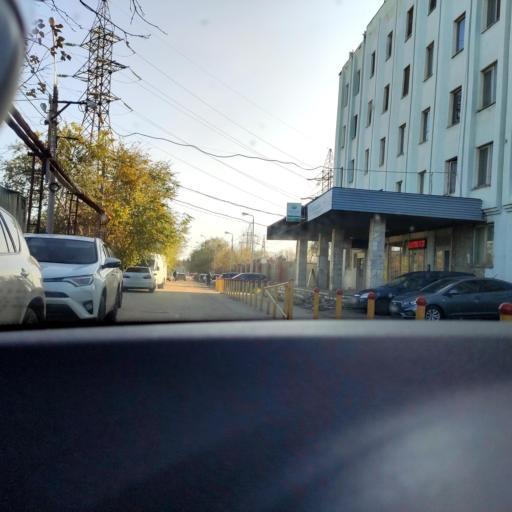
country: RU
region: Samara
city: Samara
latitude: 53.2098
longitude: 50.2718
